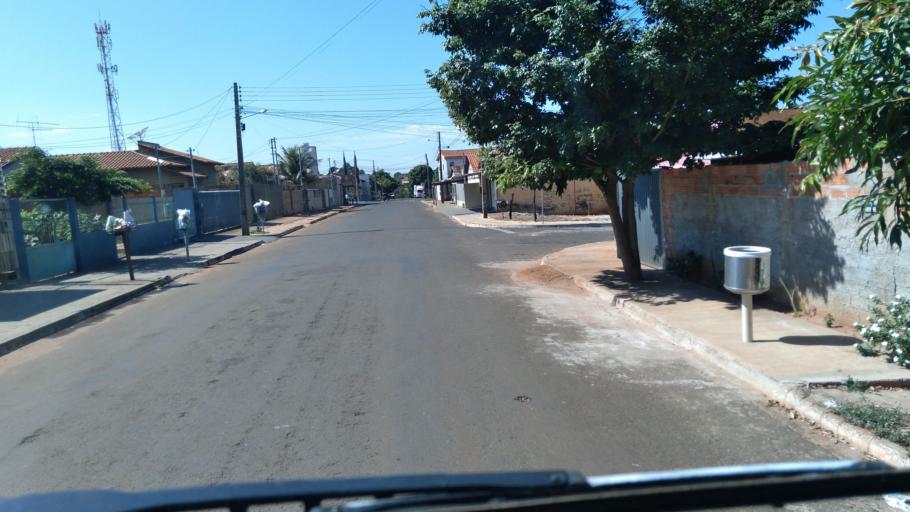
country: BR
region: Goias
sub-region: Mineiros
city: Mineiros
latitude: -17.5703
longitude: -52.5667
